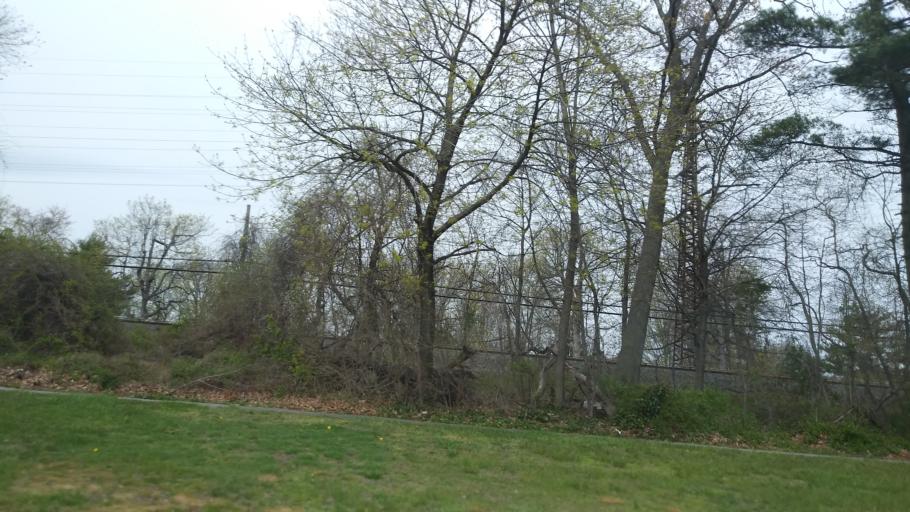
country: US
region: New York
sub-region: Nassau County
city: Rockville Centre
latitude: 40.6572
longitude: -73.6276
